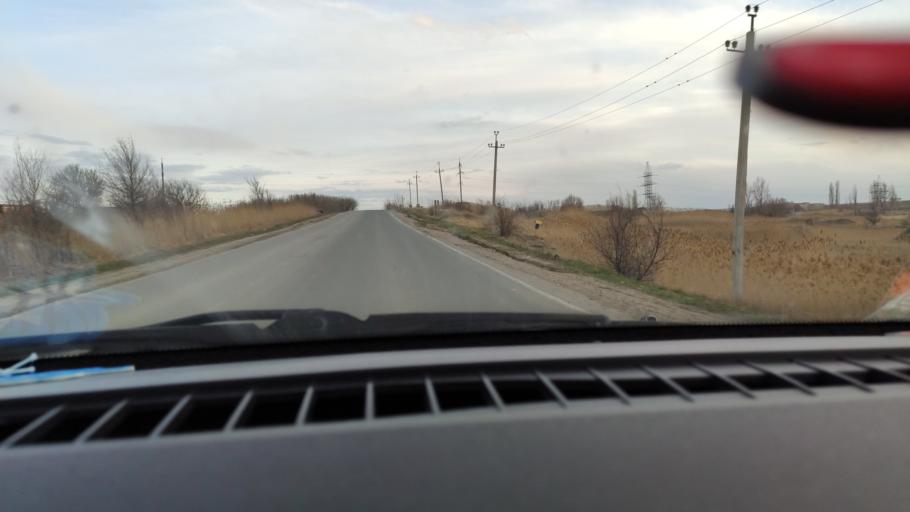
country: RU
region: Saratov
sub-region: Saratovskiy Rayon
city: Saratov
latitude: 51.6158
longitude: 45.9494
